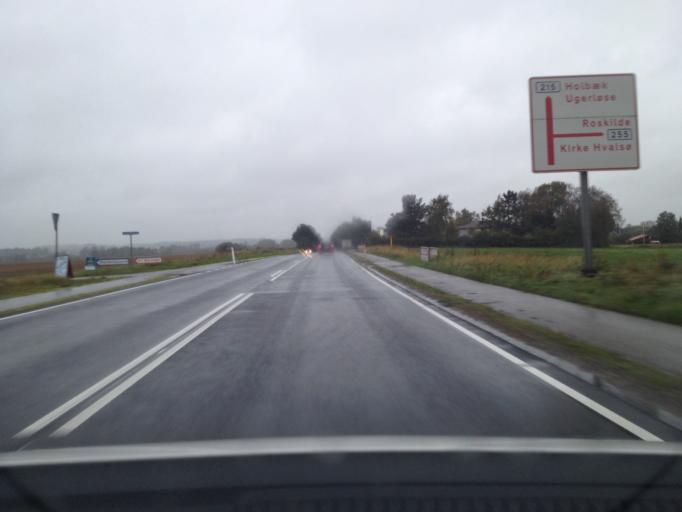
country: DK
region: Zealand
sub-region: Holbaek Kommune
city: Tollose
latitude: 55.5393
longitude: 11.7114
